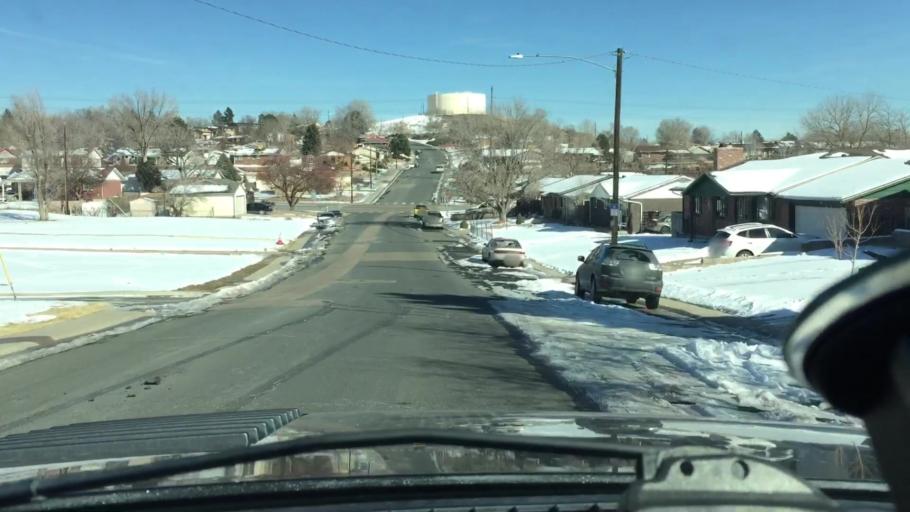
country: US
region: Colorado
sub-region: Adams County
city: Sherrelwood
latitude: 39.8387
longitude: -105.0022
